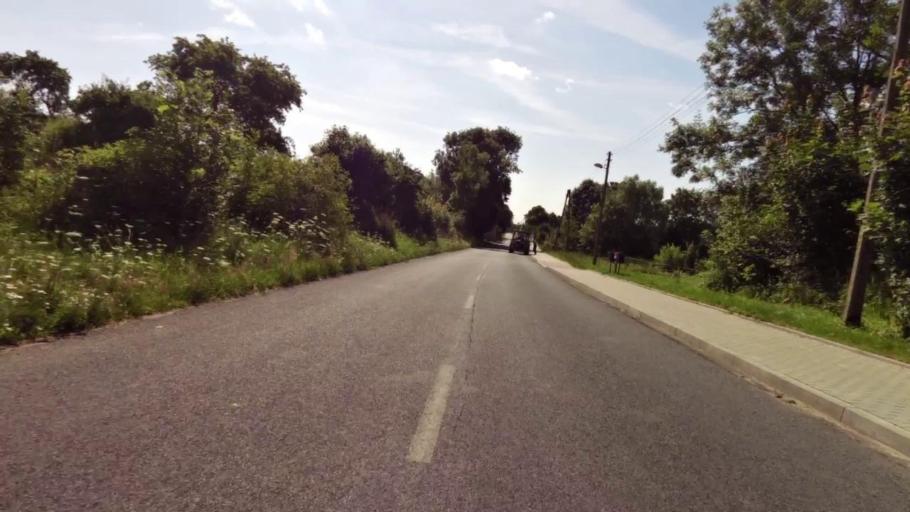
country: PL
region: West Pomeranian Voivodeship
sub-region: Powiat stargardzki
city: Dobrzany
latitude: 53.4089
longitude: 15.4274
